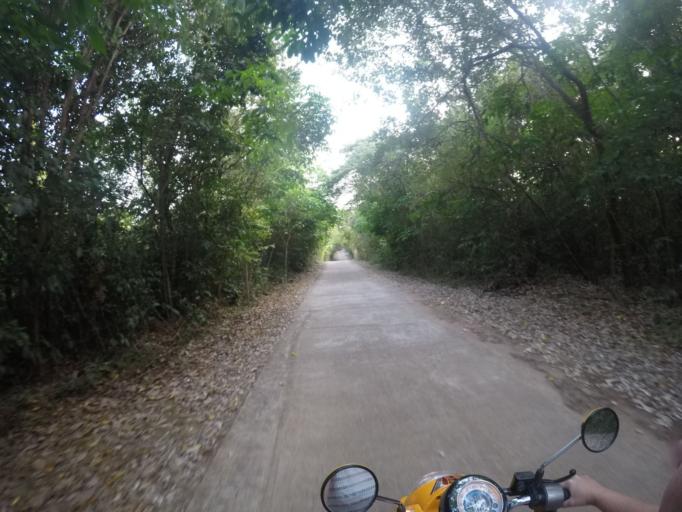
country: TH
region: Trat
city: Ko Kut
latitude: 11.8014
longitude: 102.4858
